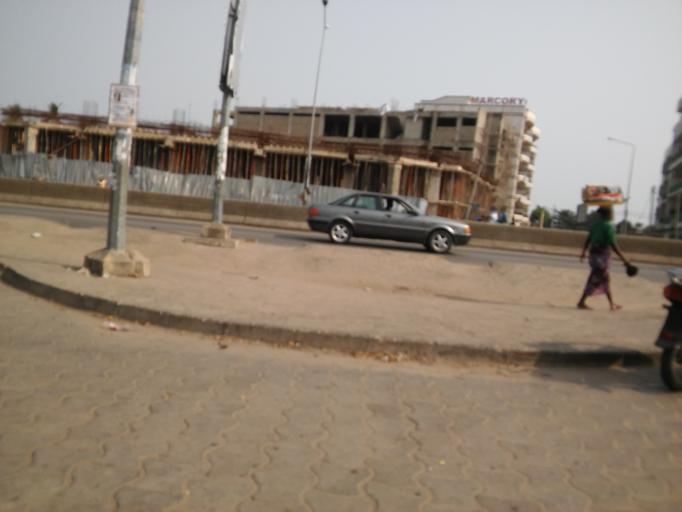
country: BJ
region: Littoral
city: Cotonou
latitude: 6.3613
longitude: 2.4446
